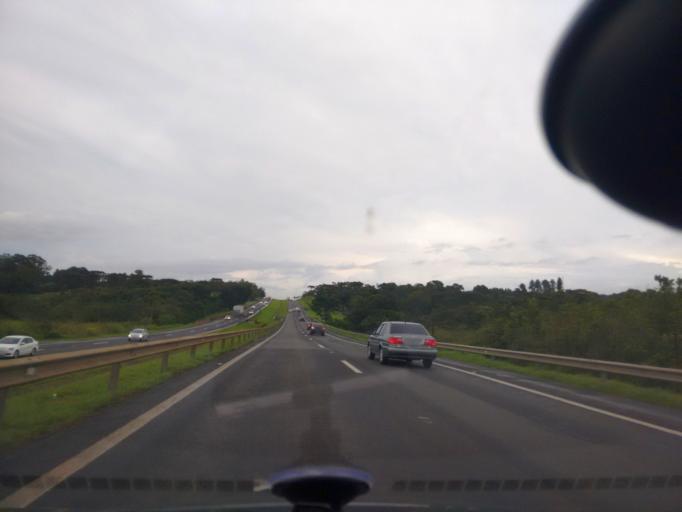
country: BR
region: Sao Paulo
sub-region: Sao Carlos
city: Sao Carlos
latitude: -22.0882
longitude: -47.8339
